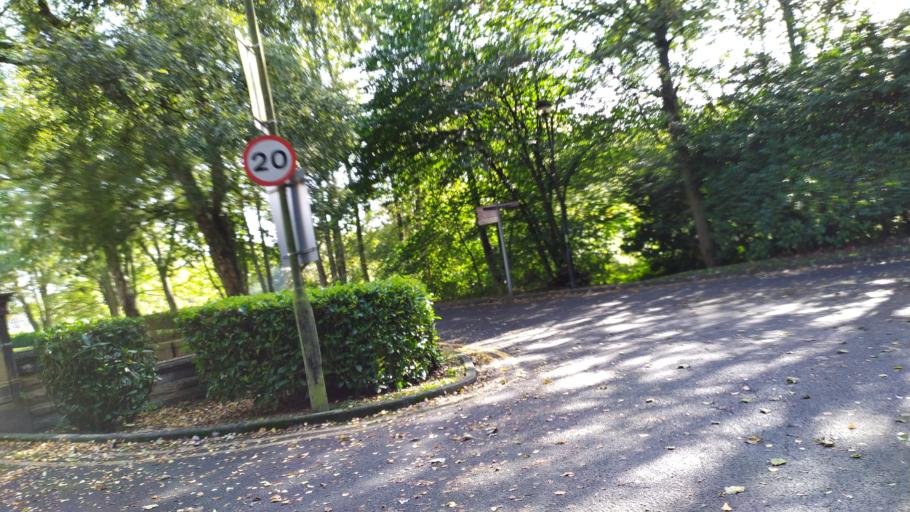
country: GB
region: England
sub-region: City and Borough of Leeds
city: Horsforth
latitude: 53.8256
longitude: -1.5950
